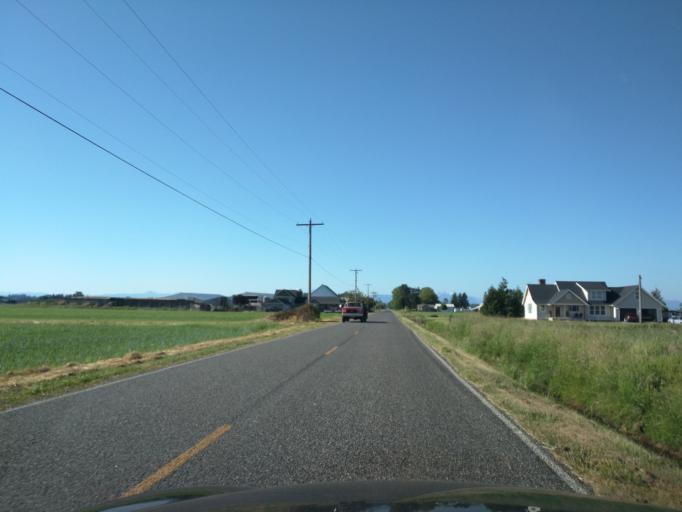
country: US
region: Washington
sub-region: Whatcom County
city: Lynden
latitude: 48.9674
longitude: -122.4410
